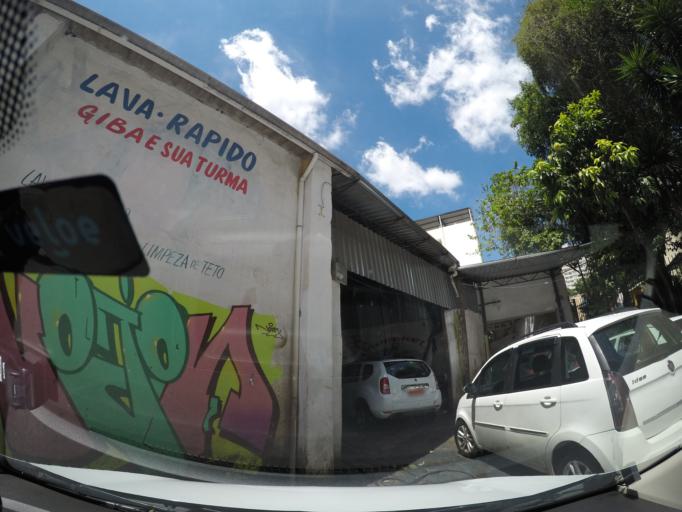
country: BR
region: Sao Paulo
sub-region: Sao Paulo
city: Sao Paulo
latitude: -23.5612
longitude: -46.6488
